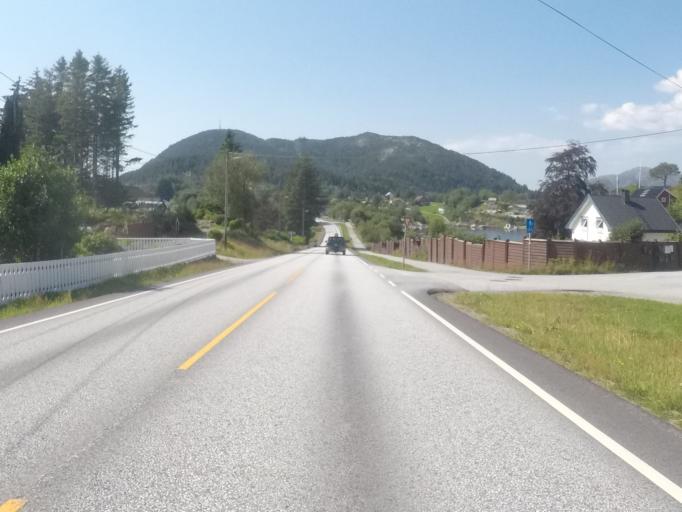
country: NO
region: Sogn og Fjordane
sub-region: Flora
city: Floro
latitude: 61.6021
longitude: 5.1456
